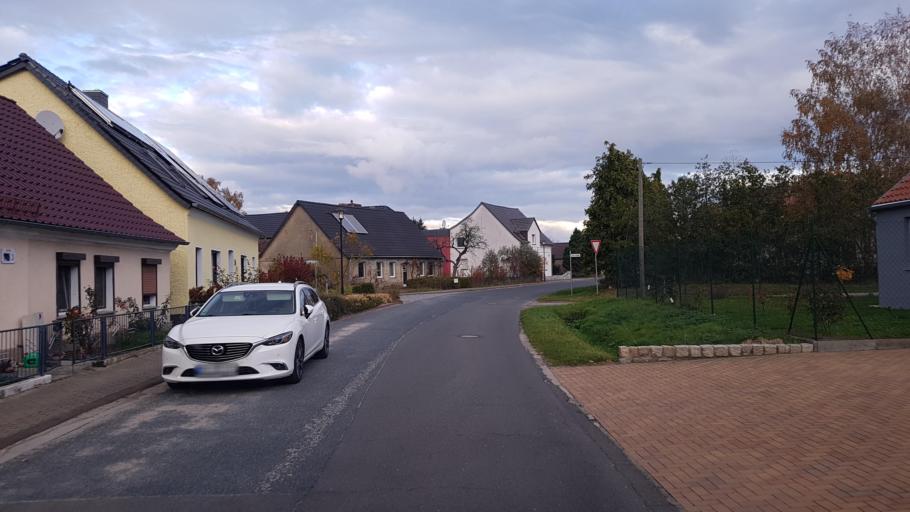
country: DE
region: Saxony-Anhalt
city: Zahna
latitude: 51.9471
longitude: 12.8330
